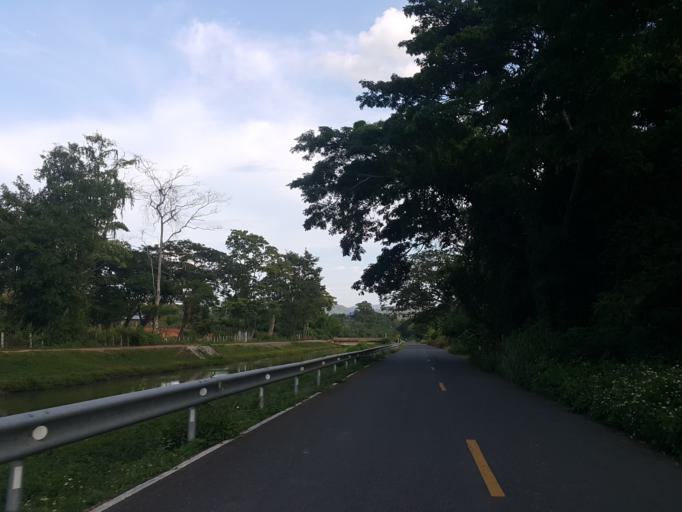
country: TH
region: Chiang Mai
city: Mae Taeng
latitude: 19.0595
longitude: 98.9679
